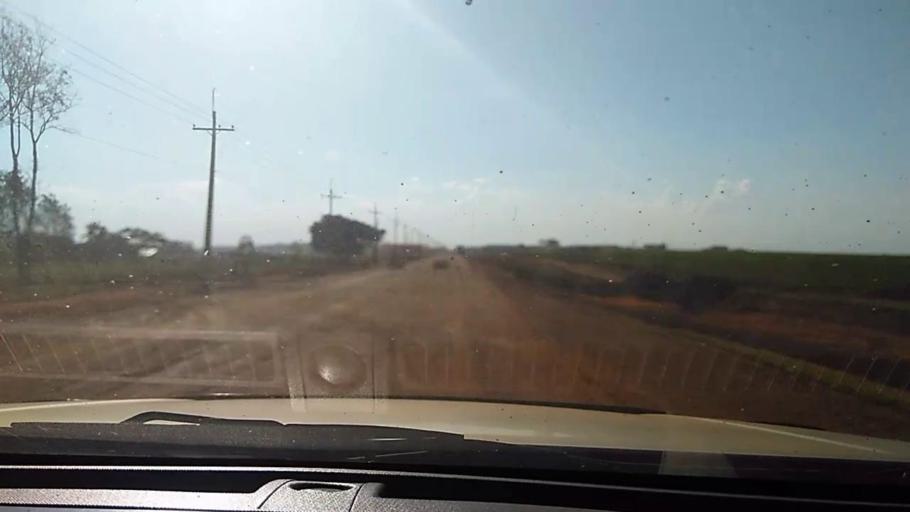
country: PY
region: Alto Parana
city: Naranjal
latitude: -25.9081
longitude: -55.4460
